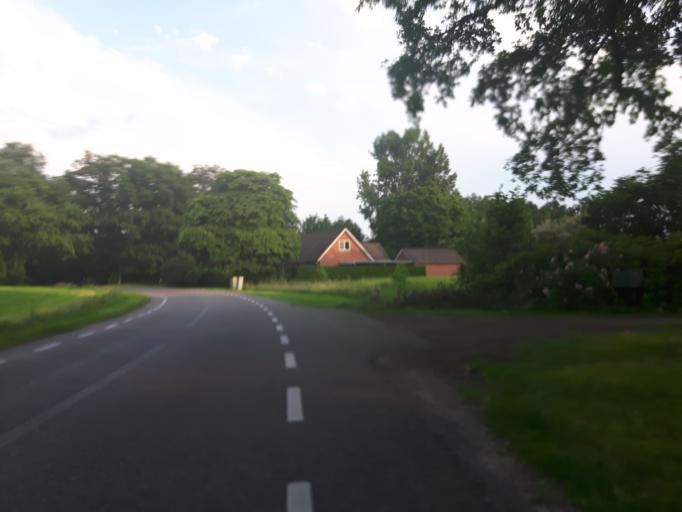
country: NL
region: Overijssel
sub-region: Gemeente Hengelo
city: Hengelo
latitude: 52.2314
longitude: 6.8293
